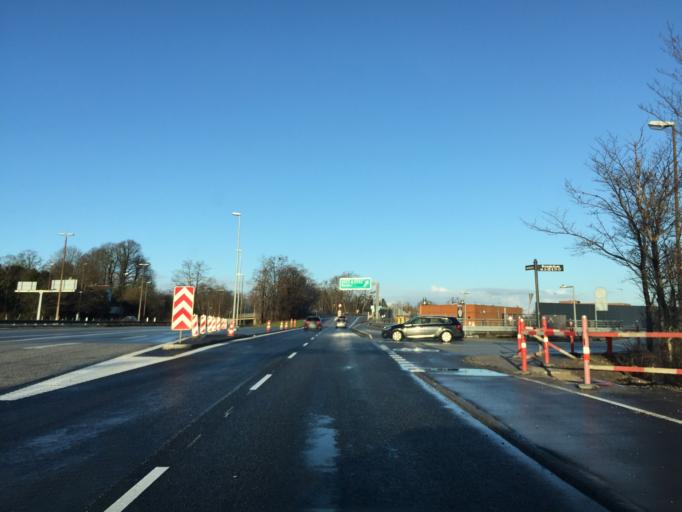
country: DK
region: Capital Region
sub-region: Lyngby-Tarbaek Kommune
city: Kongens Lyngby
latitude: 55.7587
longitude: 12.5174
